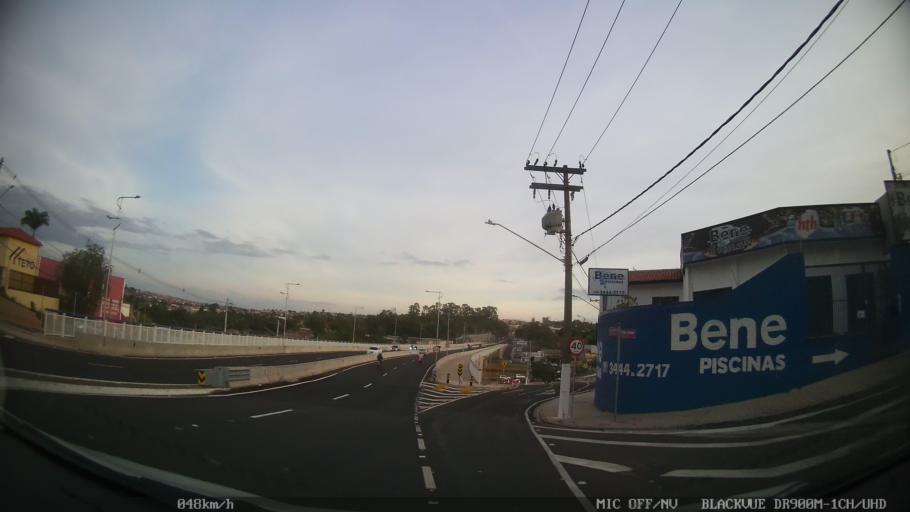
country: BR
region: Sao Paulo
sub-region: Limeira
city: Limeira
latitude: -22.5825
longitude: -47.4095
